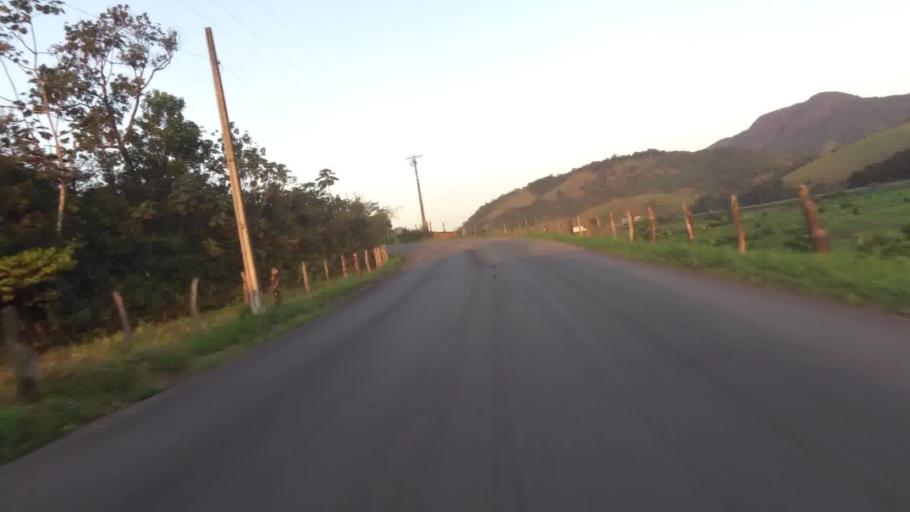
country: BR
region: Espirito Santo
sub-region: Alfredo Chaves
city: Alfredo Chaves
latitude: -20.6513
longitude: -40.6455
